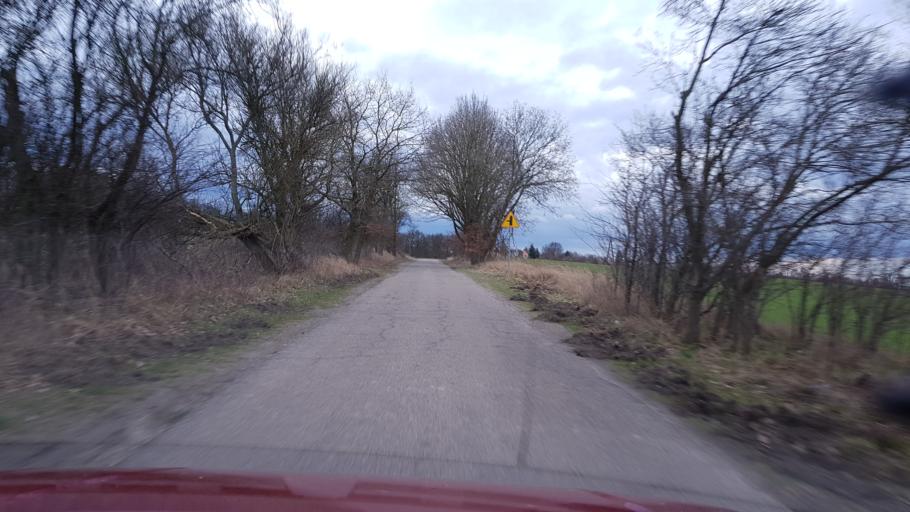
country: PL
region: West Pomeranian Voivodeship
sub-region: Powiat gryfinski
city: Stare Czarnowo
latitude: 53.3295
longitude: 14.6737
